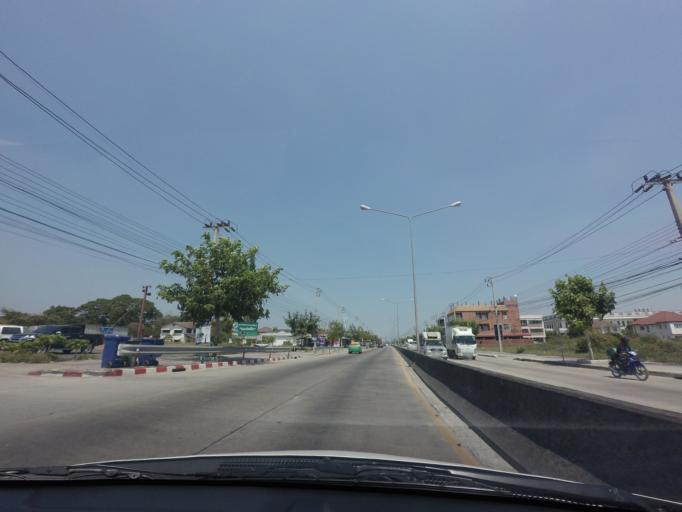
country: TH
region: Bangkok
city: Khlong Sam Wa
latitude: 13.8350
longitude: 100.7763
